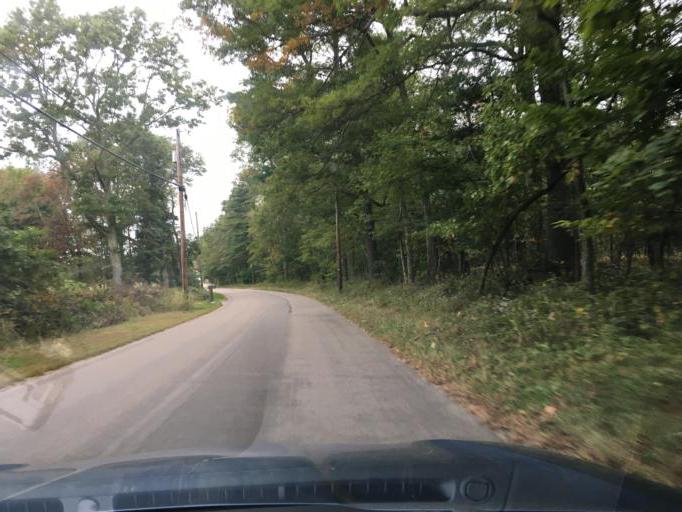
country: US
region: Rhode Island
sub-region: Washington County
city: Exeter
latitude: 41.5890
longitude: -71.5590
